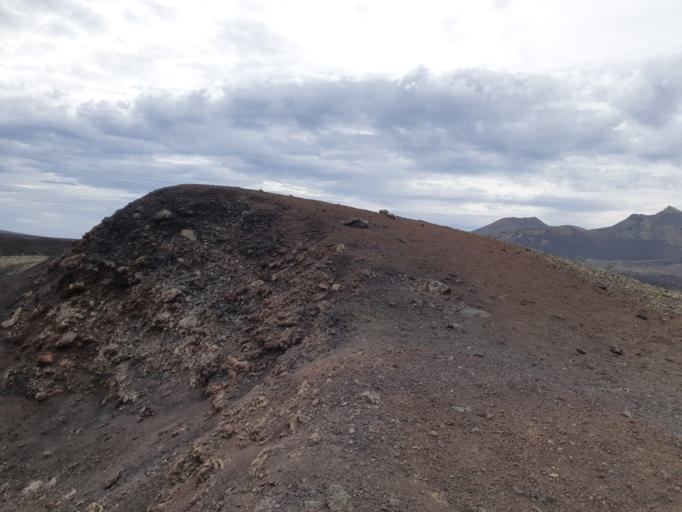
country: ES
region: Canary Islands
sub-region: Provincia de Las Palmas
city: Tinajo
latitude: 29.0218
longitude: -13.7130
